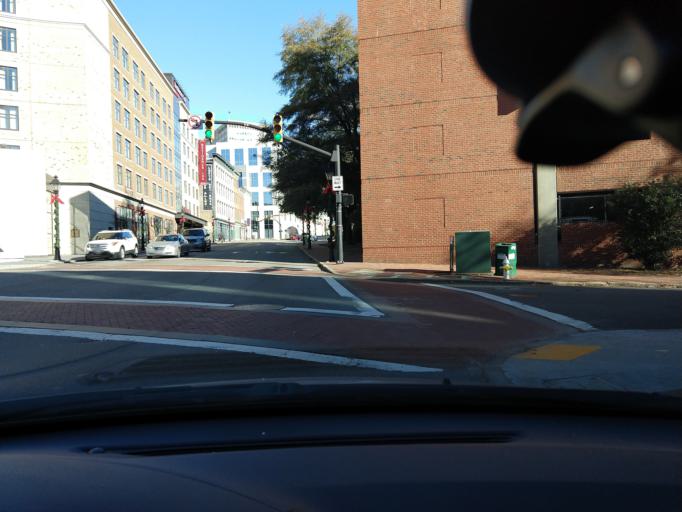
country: US
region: Virginia
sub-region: City of Richmond
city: Richmond
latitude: 37.5343
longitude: -77.4325
